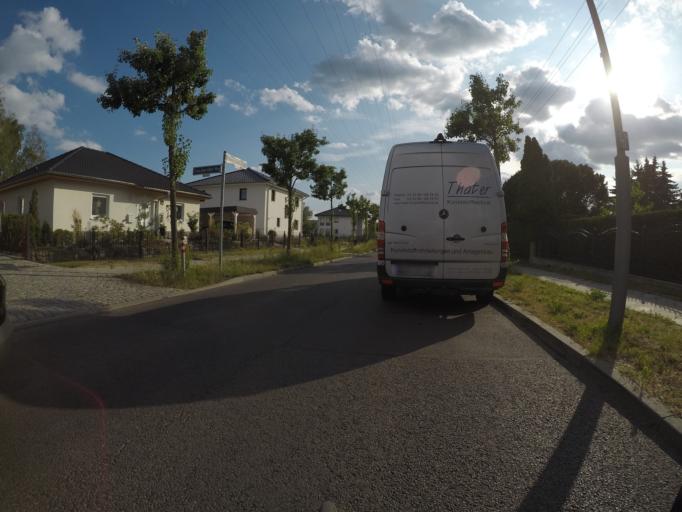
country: DE
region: Berlin
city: Hellersdorf
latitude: 52.5227
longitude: 13.6021
